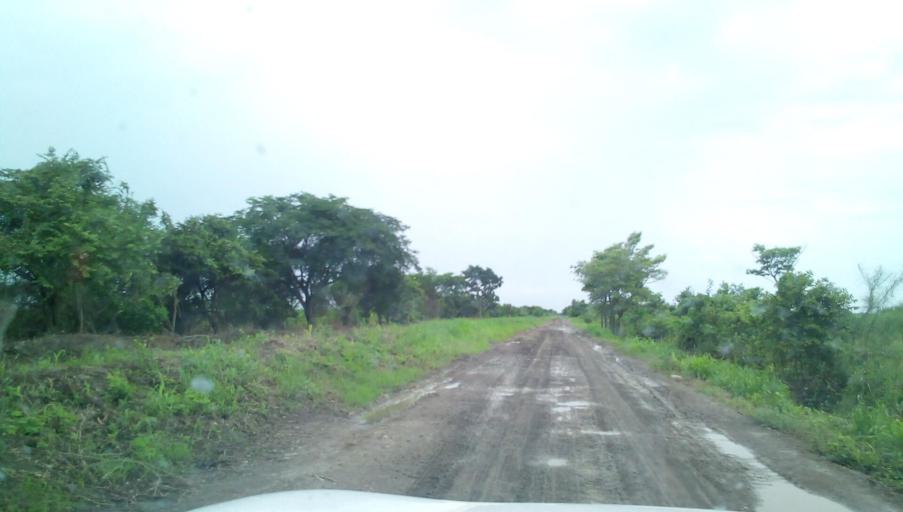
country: MX
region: Veracruz
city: Panuco
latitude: 21.8269
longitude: -98.1108
